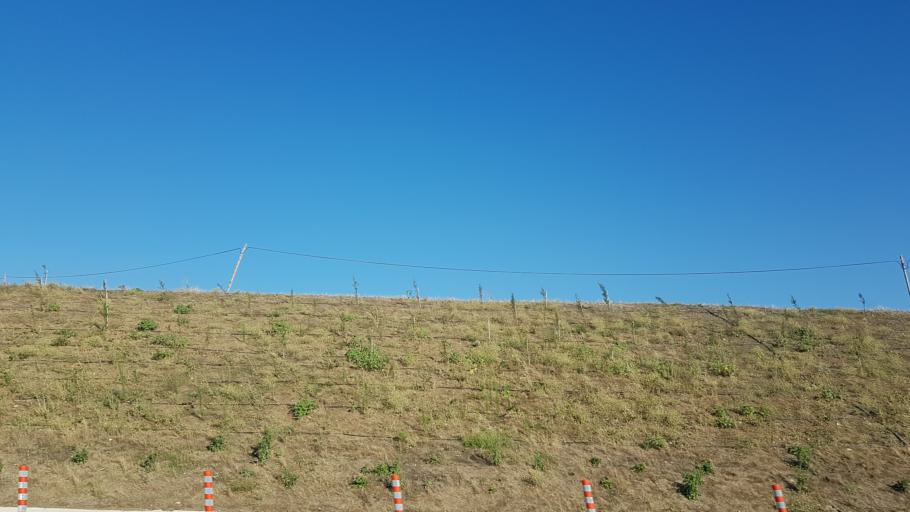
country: TR
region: Balikesir
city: Ertugrul
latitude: 39.6717
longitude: 27.7438
